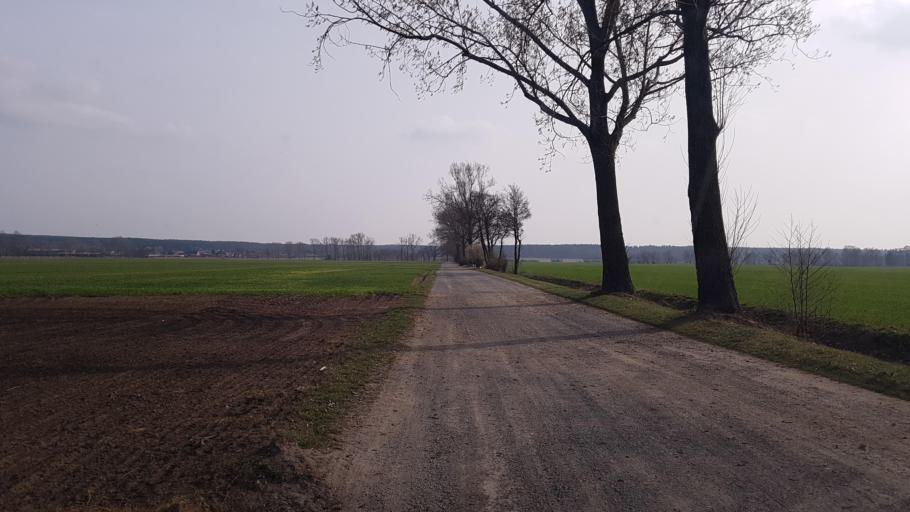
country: DE
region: Brandenburg
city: Merzdorf
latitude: 51.4174
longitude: 13.5265
